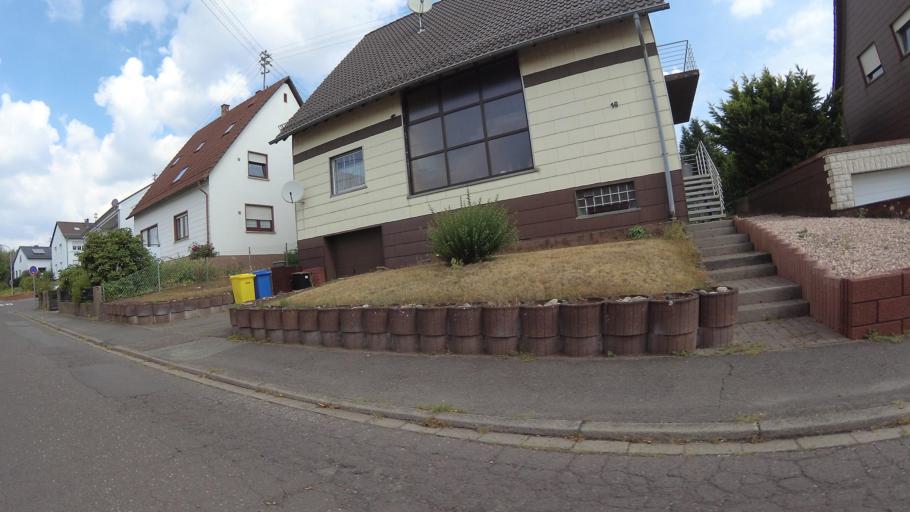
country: DE
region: Rheinland-Pfalz
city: Grossbundenbach
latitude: 49.3026
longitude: 7.3990
